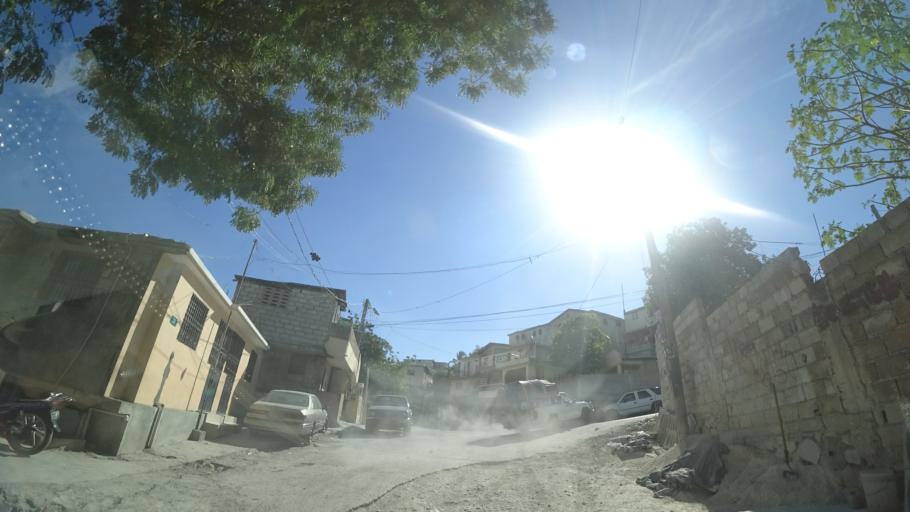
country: HT
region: Ouest
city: Delmas 73
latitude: 18.5490
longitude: -72.3153
